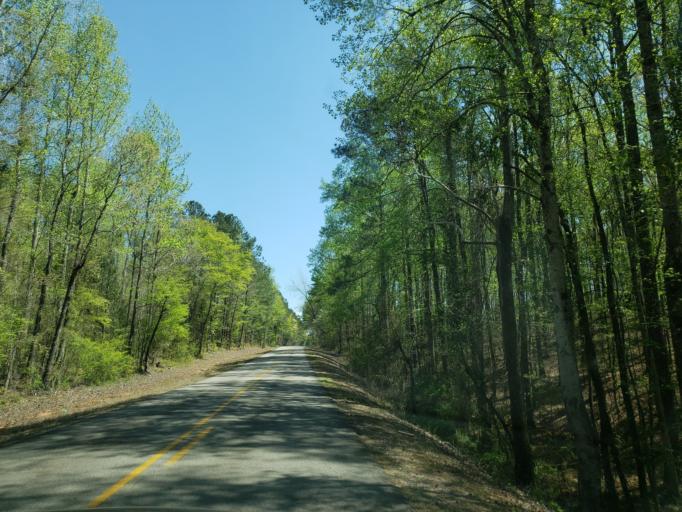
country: US
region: Alabama
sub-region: Tallapoosa County
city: Camp Hill
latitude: 32.6866
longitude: -85.6743
